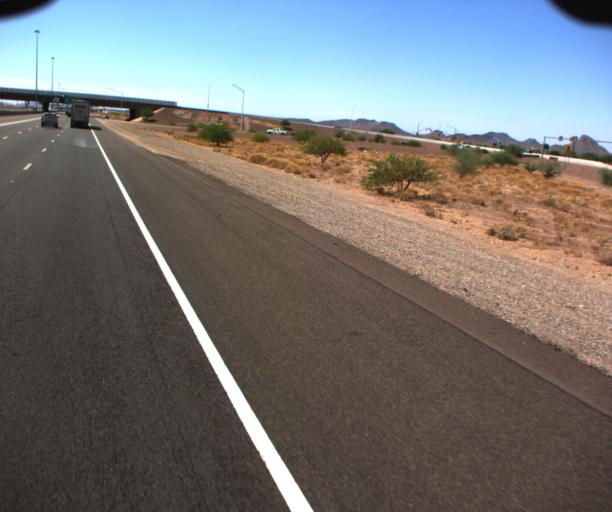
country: US
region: Arizona
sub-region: Maricopa County
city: Anthem
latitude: 33.8012
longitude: -112.1363
